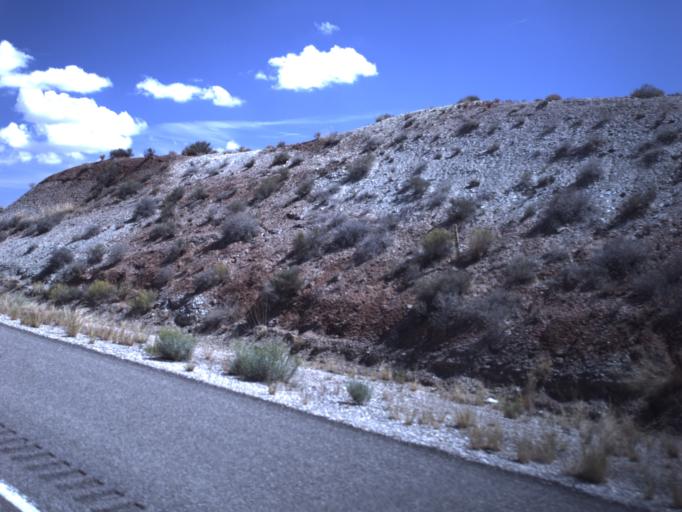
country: US
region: Utah
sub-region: Emery County
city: Ferron
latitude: 38.8468
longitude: -111.0222
